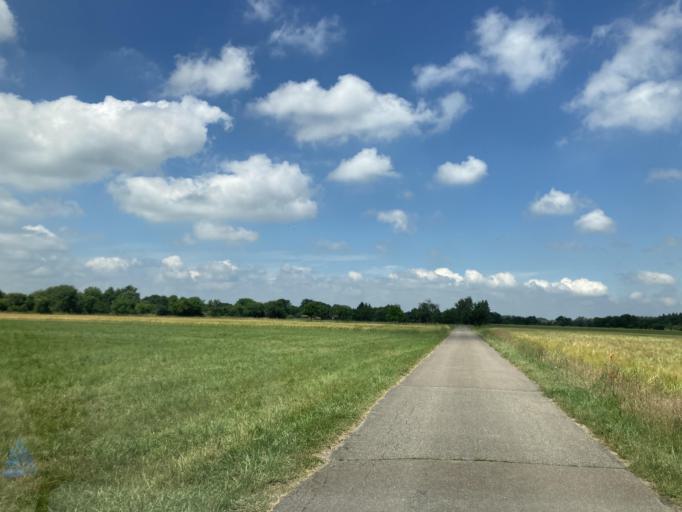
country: DE
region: Baden-Wuerttemberg
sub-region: Karlsruhe Region
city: Hambrucken
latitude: 49.1754
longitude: 8.5198
